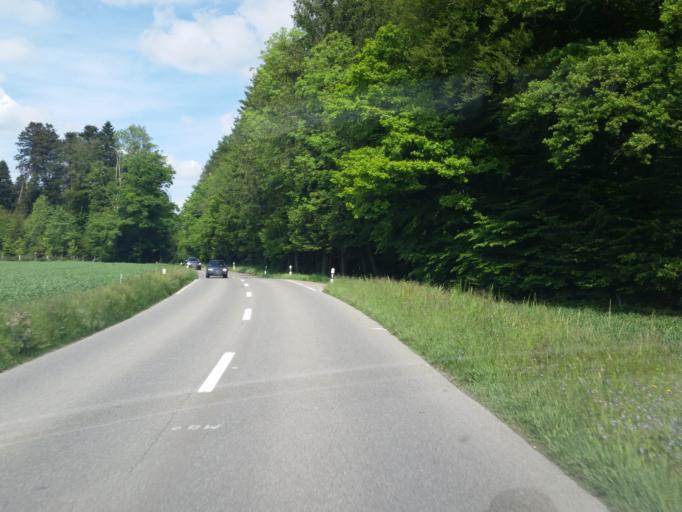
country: CH
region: Aargau
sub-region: Bezirk Muri
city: Waltenschwil
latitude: 47.3350
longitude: 8.3195
